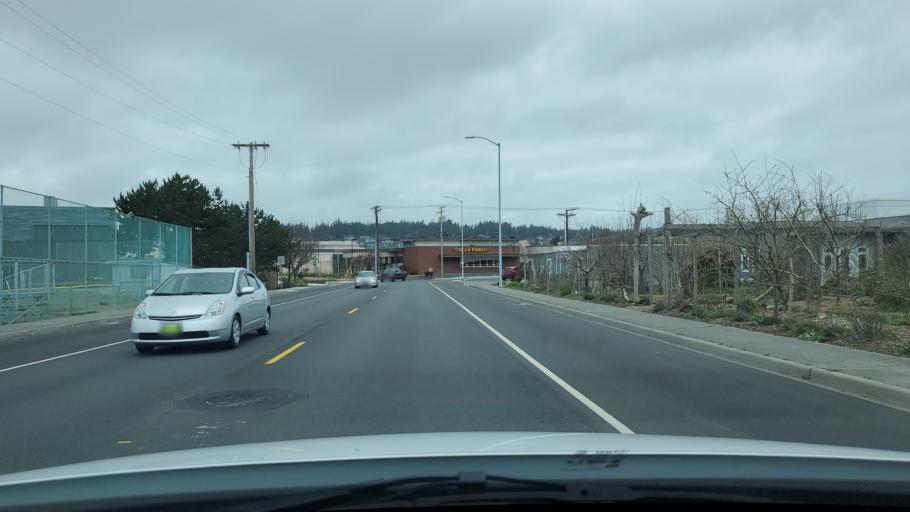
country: US
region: Washington
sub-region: Island County
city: Oak Harbor
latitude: 48.2874
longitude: -122.6511
